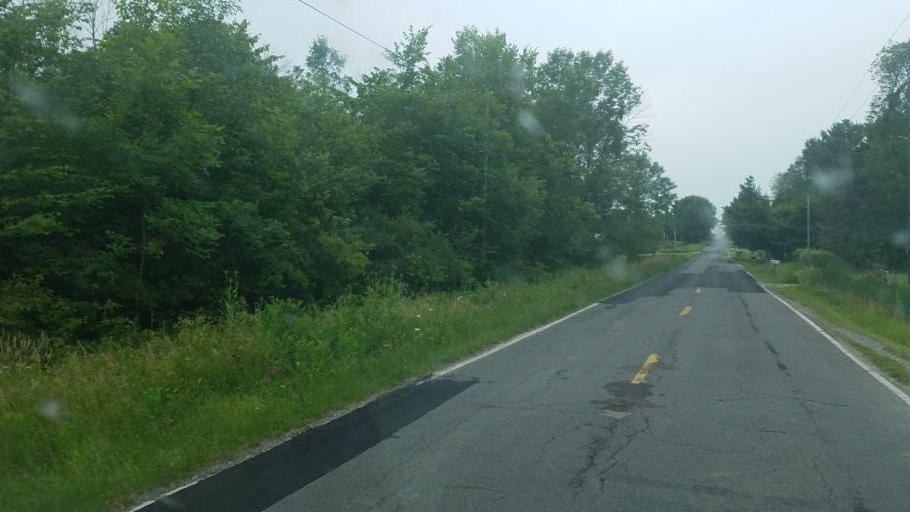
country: US
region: Ohio
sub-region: Trumbull County
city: South Canal
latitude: 41.1707
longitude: -81.0280
